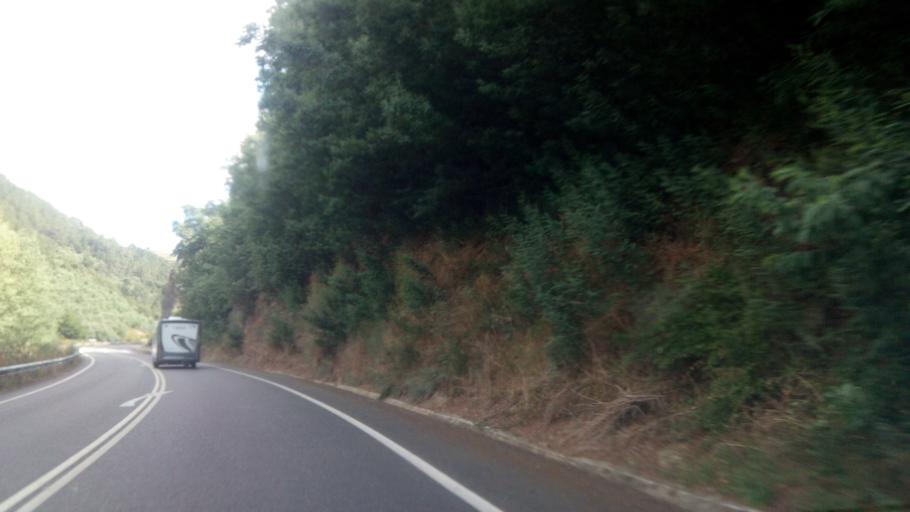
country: ES
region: Galicia
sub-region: Provincia de Ourense
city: Nogueira de Ramuin
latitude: 42.4217
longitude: -7.7665
